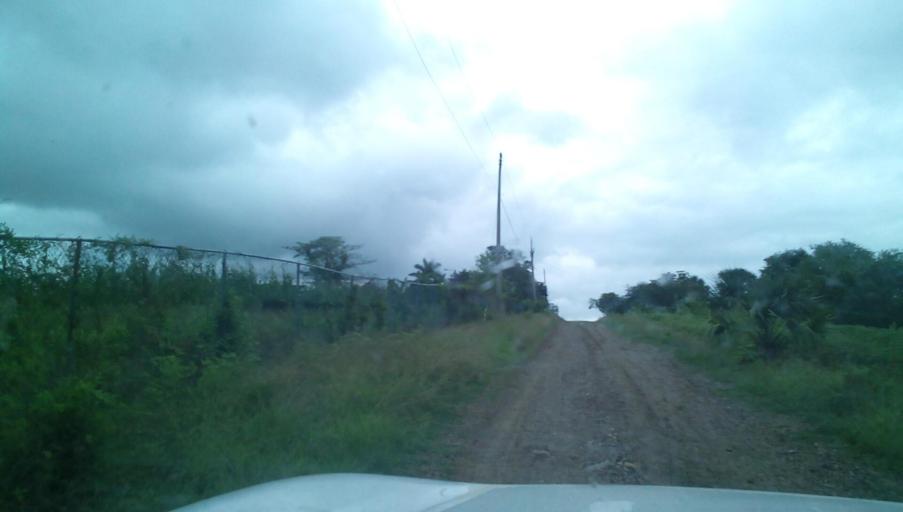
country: MX
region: Veracruz
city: Panuco
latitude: 21.8019
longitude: -98.1082
